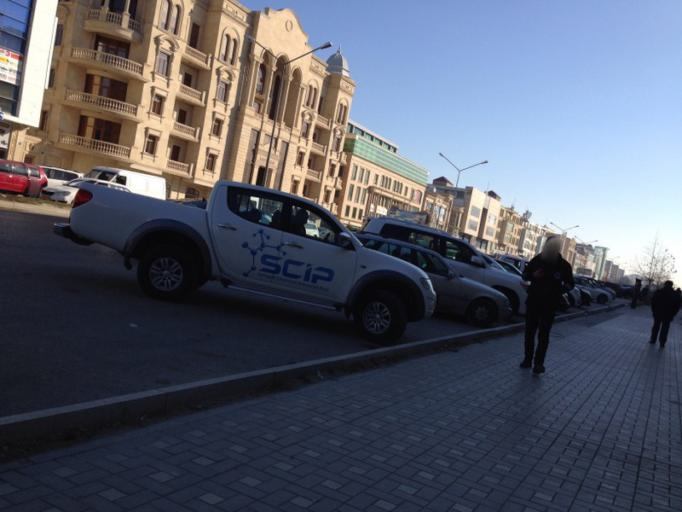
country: AZ
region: Baki
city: Baku
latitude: 40.4131
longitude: 49.8606
